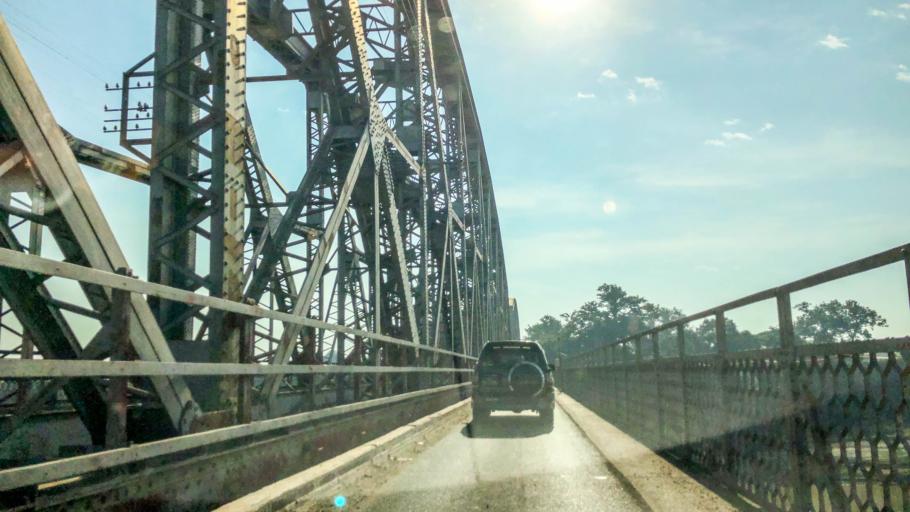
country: MM
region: Sagain
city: Sagaing
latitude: 21.8696
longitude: 95.9941
